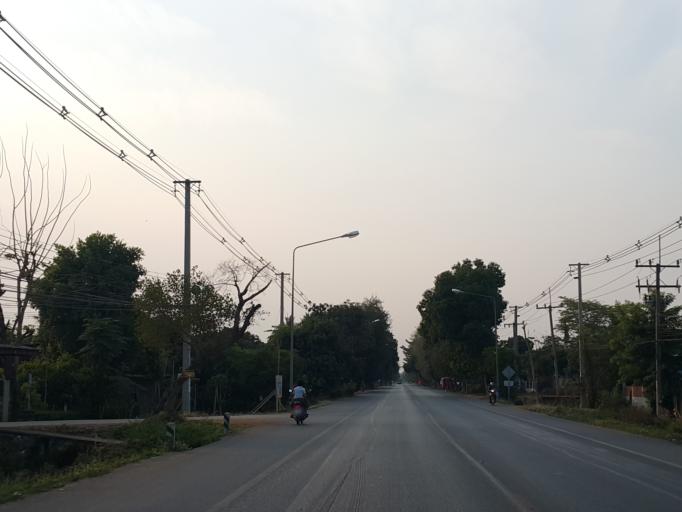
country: TH
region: Sukhothai
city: Si Samrong
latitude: 17.2148
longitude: 99.8649
